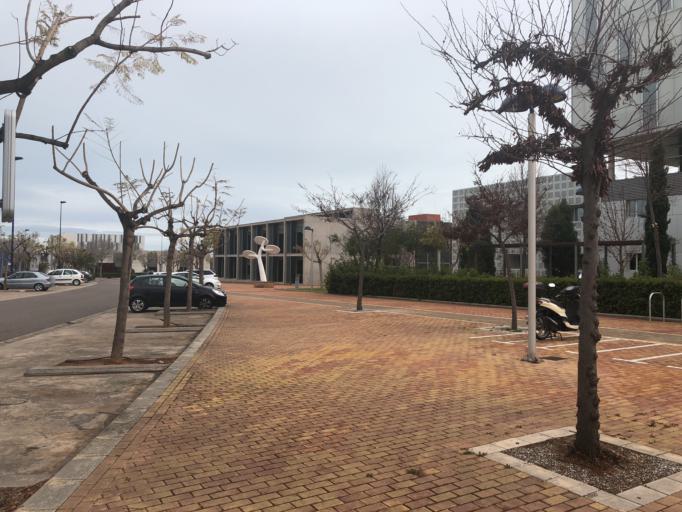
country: ES
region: Valencia
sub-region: Provincia de Castello
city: Castello de la Plana
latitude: 39.9942
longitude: -0.0737
